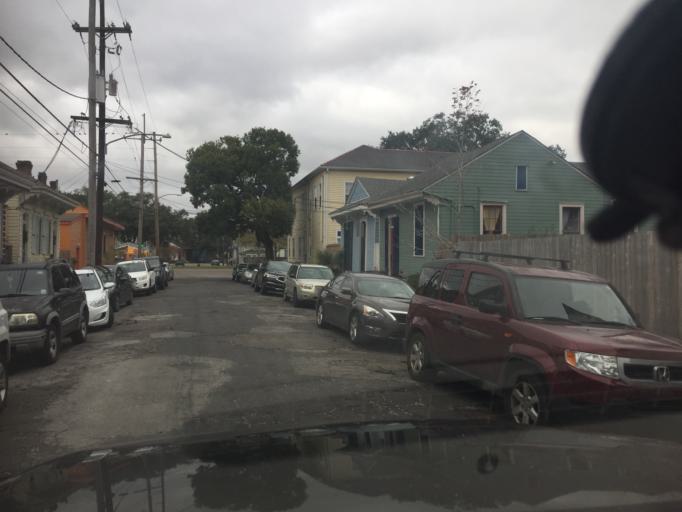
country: US
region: Louisiana
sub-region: Orleans Parish
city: New Orleans
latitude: 29.9772
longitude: -90.0761
